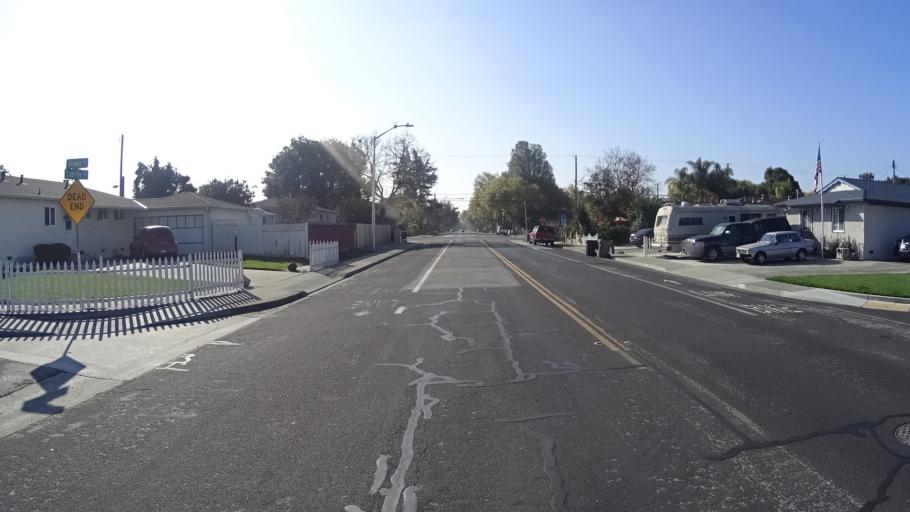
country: US
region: California
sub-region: Santa Clara County
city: Santa Clara
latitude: 37.3602
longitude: -121.9785
